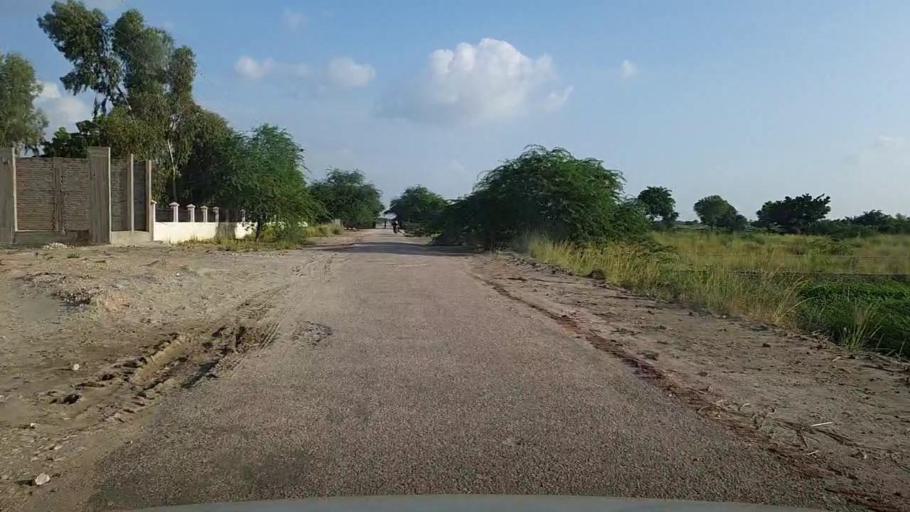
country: PK
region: Sindh
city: Hingorja
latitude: 27.0824
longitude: 68.4188
